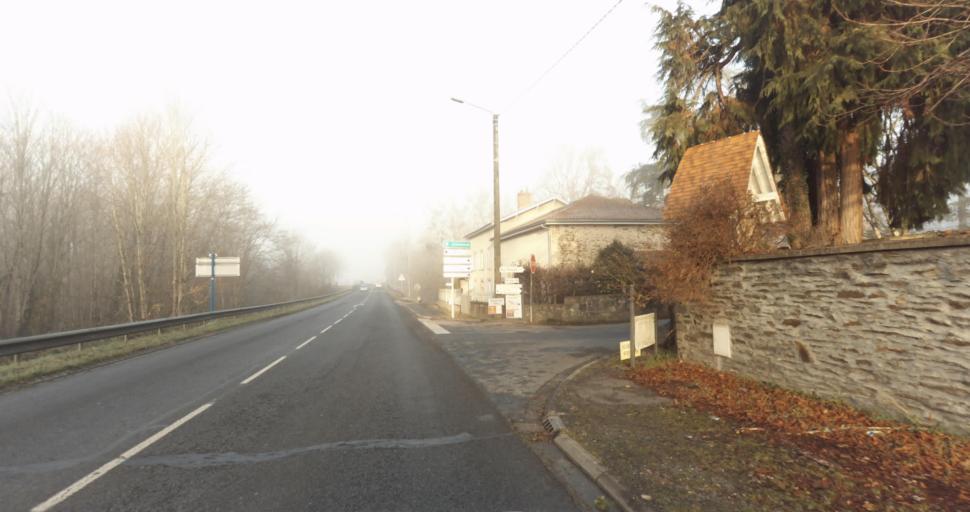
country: FR
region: Limousin
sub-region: Departement de la Haute-Vienne
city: Aixe-sur-Vienne
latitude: 45.7945
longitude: 1.1515
